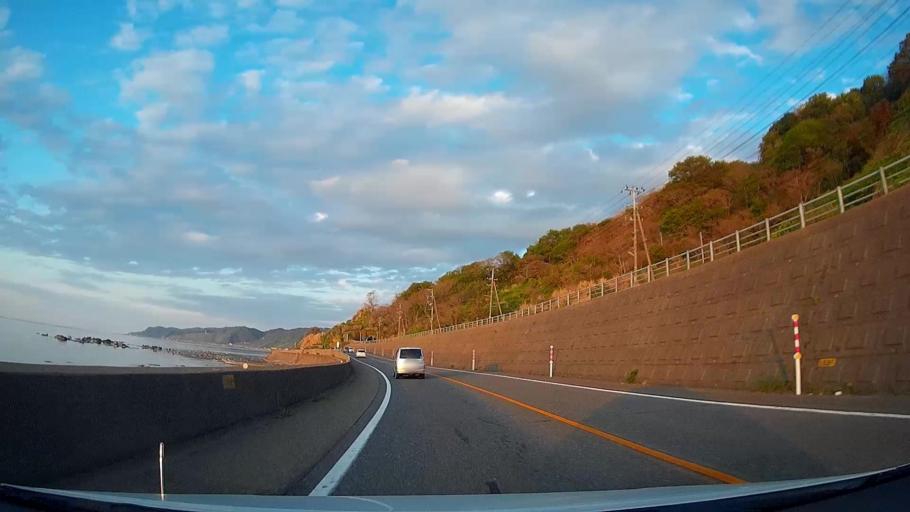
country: JP
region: Niigata
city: Itoigawa
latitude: 37.1144
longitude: 138.0091
